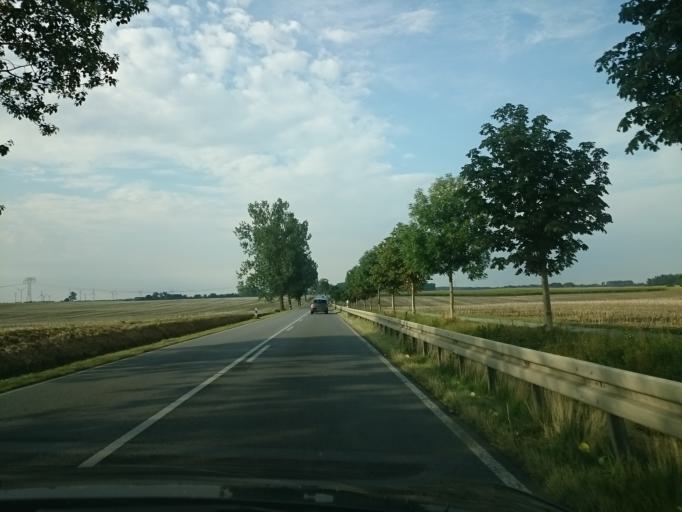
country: DE
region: Mecklenburg-Vorpommern
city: Demmin
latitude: 53.8896
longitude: 13.0324
